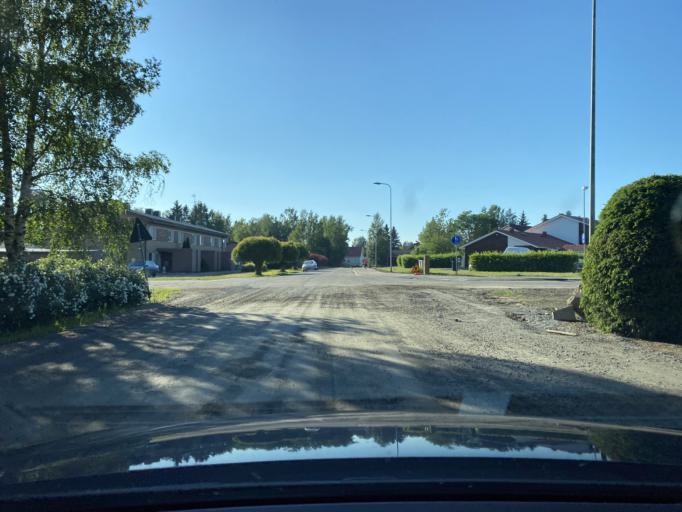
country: FI
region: Satakunta
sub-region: Pori
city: Huittinen
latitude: 61.1694
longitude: 22.7013
